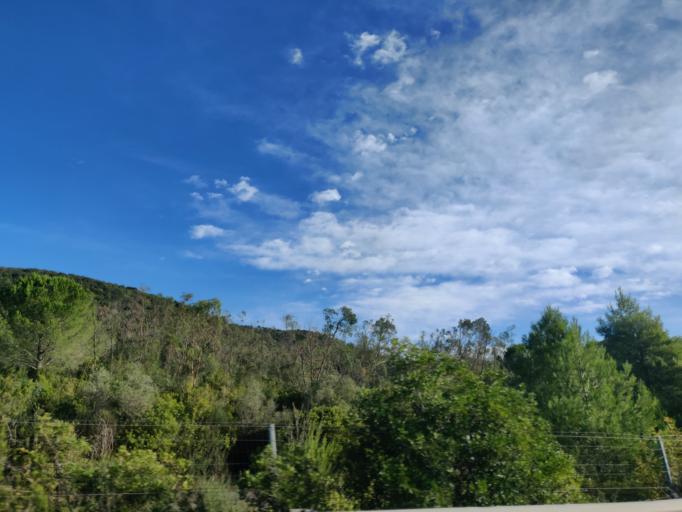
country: IT
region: Tuscany
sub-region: Provincia di Grosseto
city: Gavorrano
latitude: 42.9511
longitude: 10.9163
